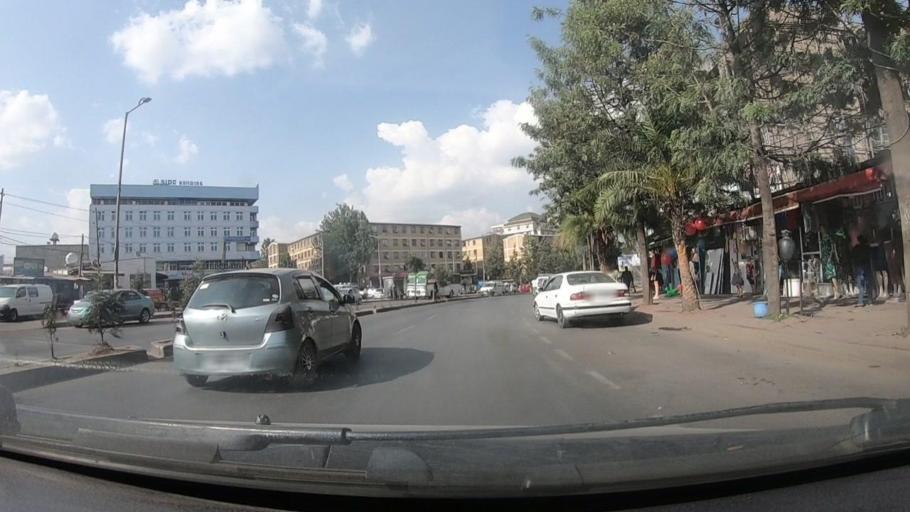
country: ET
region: Adis Abeba
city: Addis Ababa
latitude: 8.9723
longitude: 38.7311
